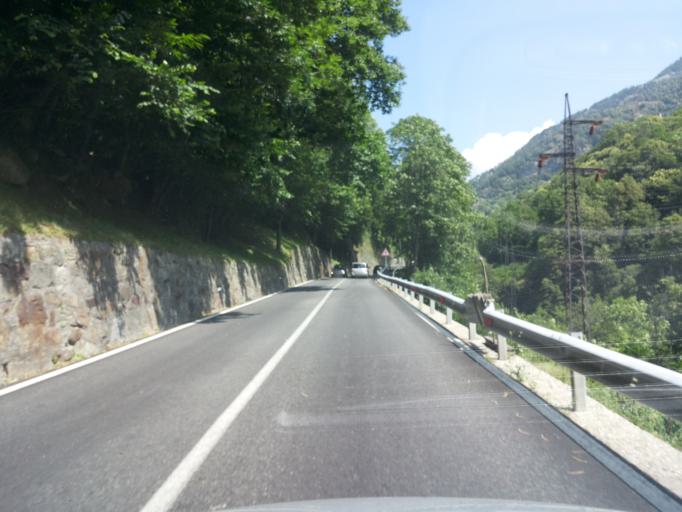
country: IT
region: Aosta Valley
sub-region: Valle d'Aosta
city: Fontainemore
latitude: 45.6644
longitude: 7.8583
